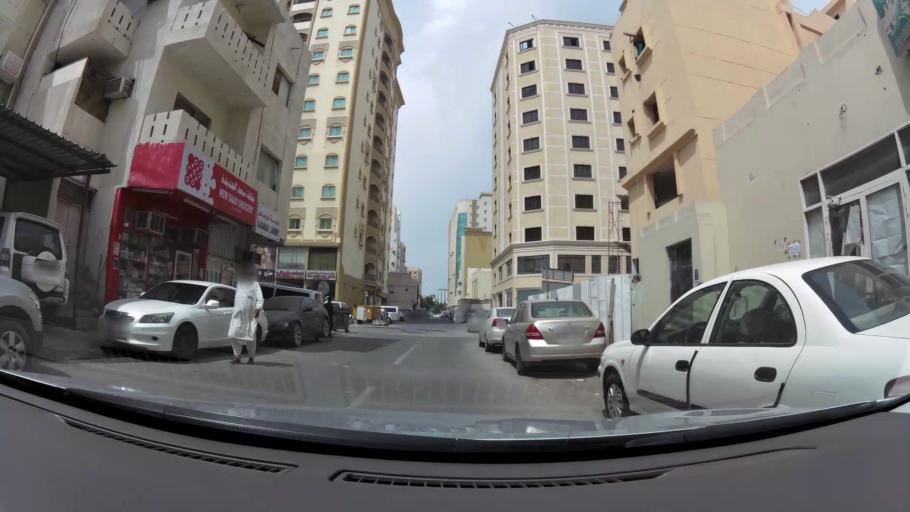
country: QA
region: Baladiyat ad Dawhah
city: Doha
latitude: 25.2762
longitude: 51.5252
